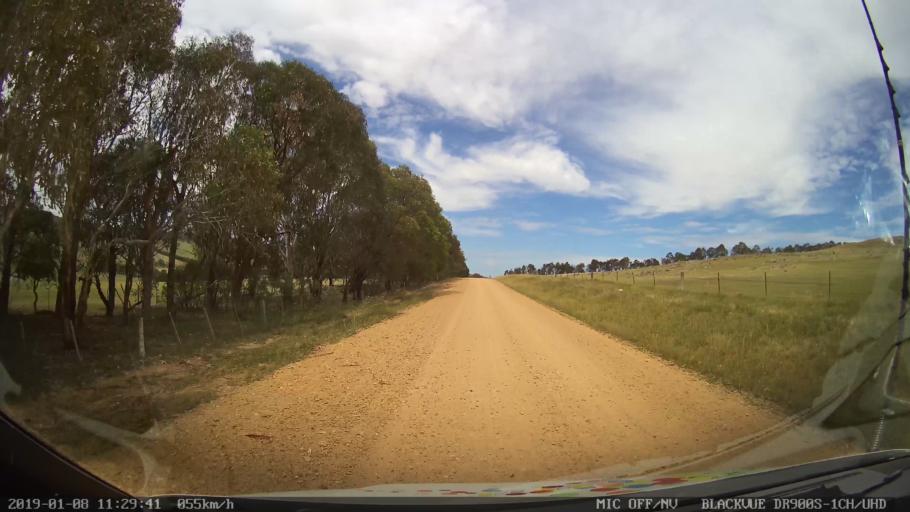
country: AU
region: New South Wales
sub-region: Guyra
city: Guyra
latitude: -30.3020
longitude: 151.5477
